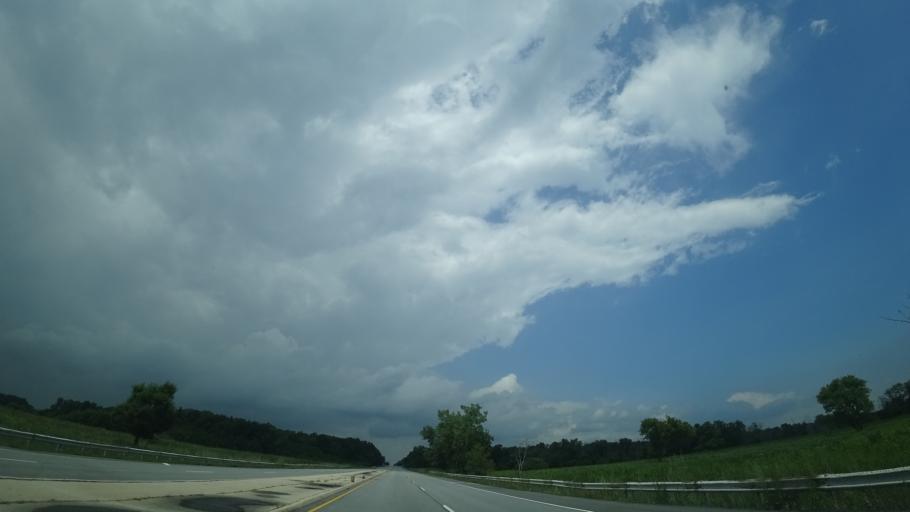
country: US
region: Illinois
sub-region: Cook County
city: Country Club Hills
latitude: 41.5367
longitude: -87.7326
